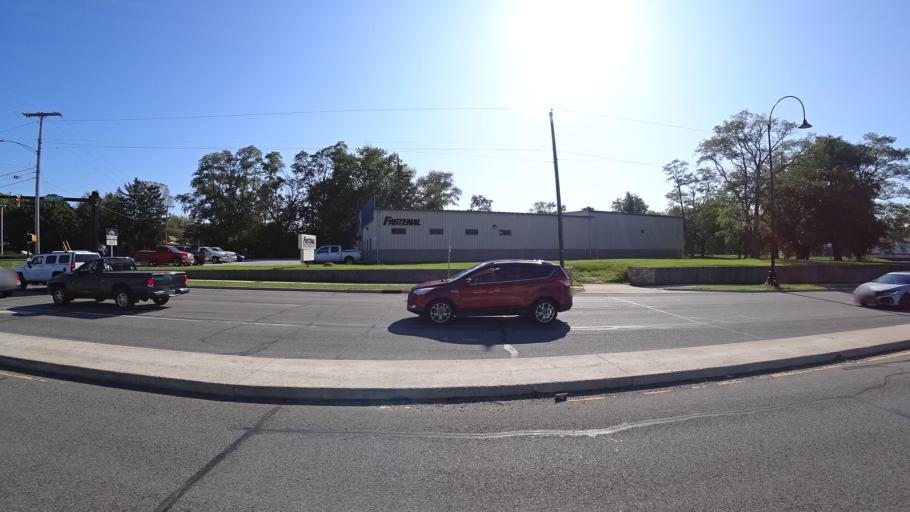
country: US
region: Indiana
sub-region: LaPorte County
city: Trail Creek
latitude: 41.7076
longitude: -86.8651
